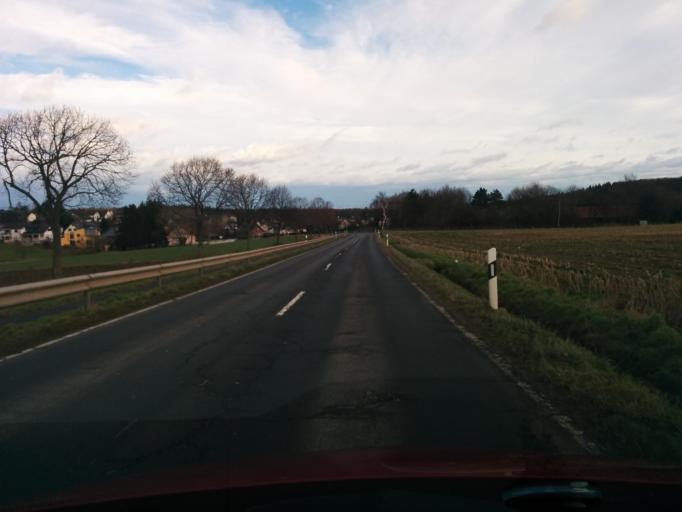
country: DE
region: North Rhine-Westphalia
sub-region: Regierungsbezirk Koln
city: Rheinbach
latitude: 50.5962
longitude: 6.9315
